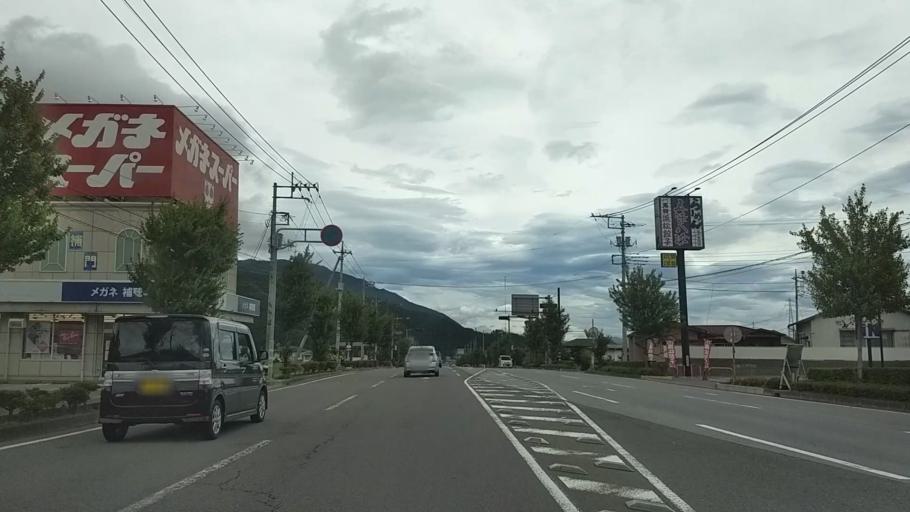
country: JP
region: Yamanashi
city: Fujikawaguchiko
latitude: 35.4916
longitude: 138.8142
